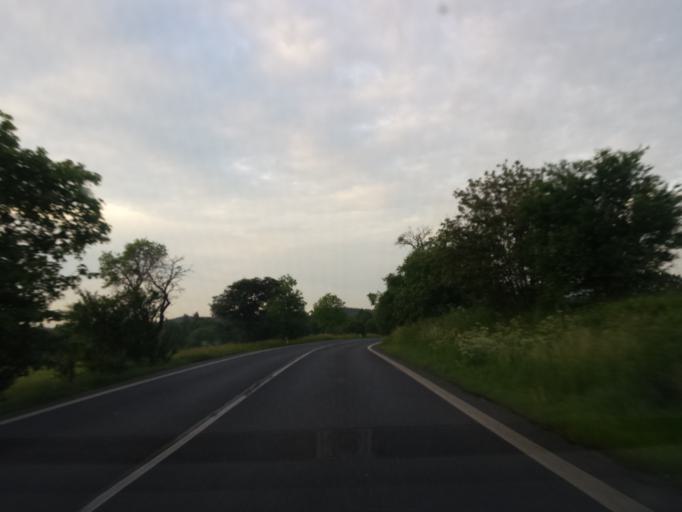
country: CZ
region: Liberecky
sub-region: Okres Ceska Lipa
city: Ceska Lipa
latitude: 50.6256
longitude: 14.5356
